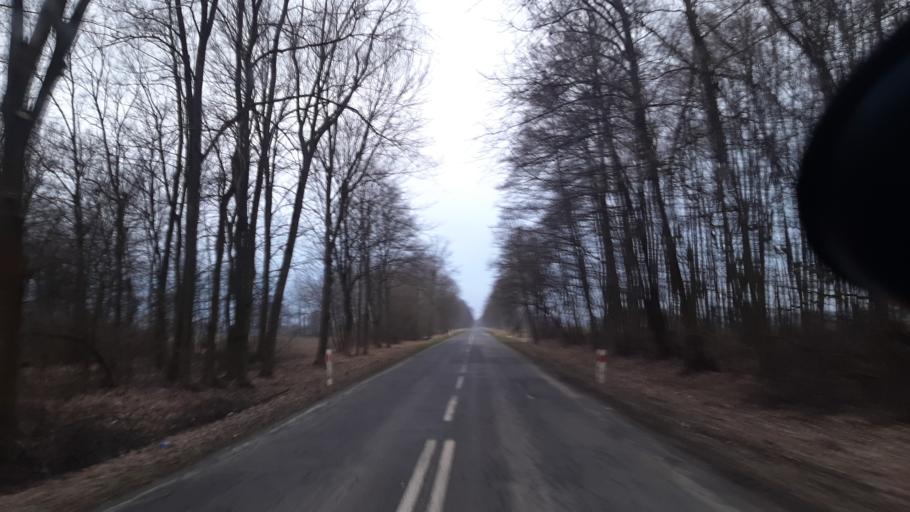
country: PL
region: Lublin Voivodeship
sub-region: Powiat parczewski
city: Sosnowica
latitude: 51.6142
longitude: 23.1176
